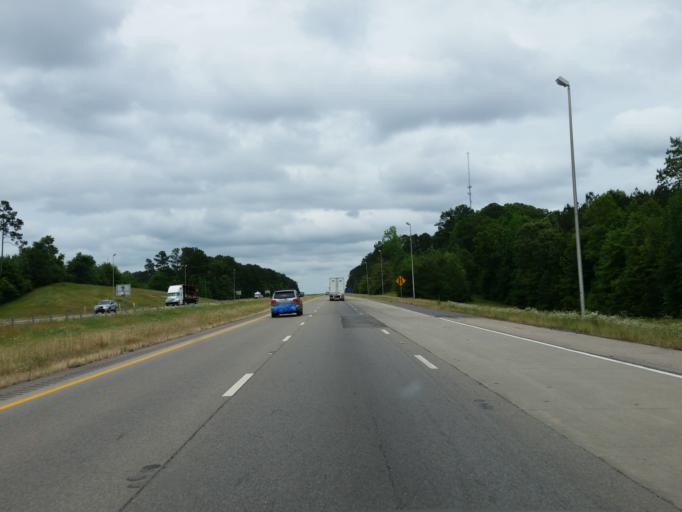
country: US
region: Alabama
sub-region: Sumter County
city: York
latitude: 32.4423
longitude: -88.4244
